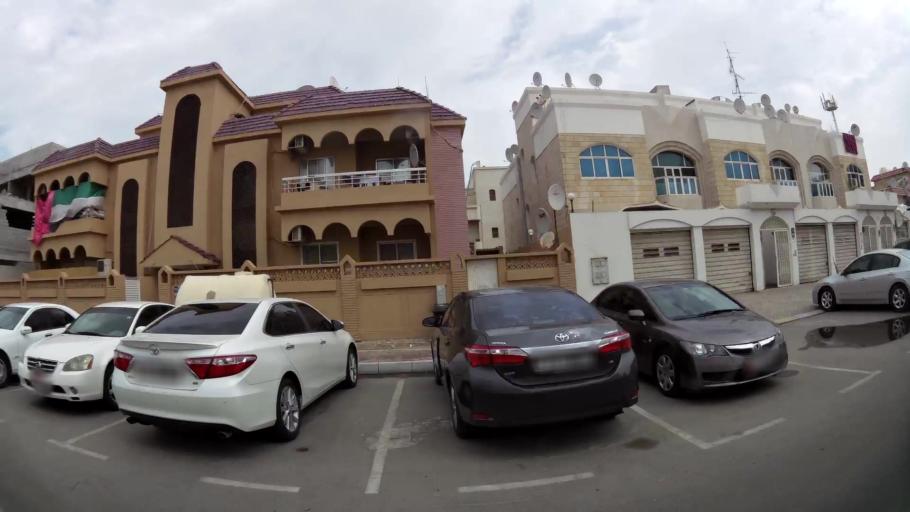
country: AE
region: Abu Dhabi
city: Abu Dhabi
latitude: 24.4376
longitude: 54.4369
